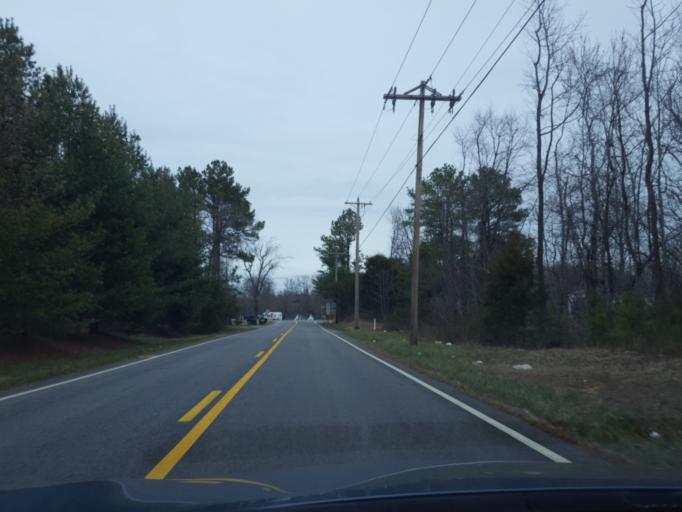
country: US
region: Maryland
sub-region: Calvert County
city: Prince Frederick
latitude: 38.5087
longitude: -76.5654
